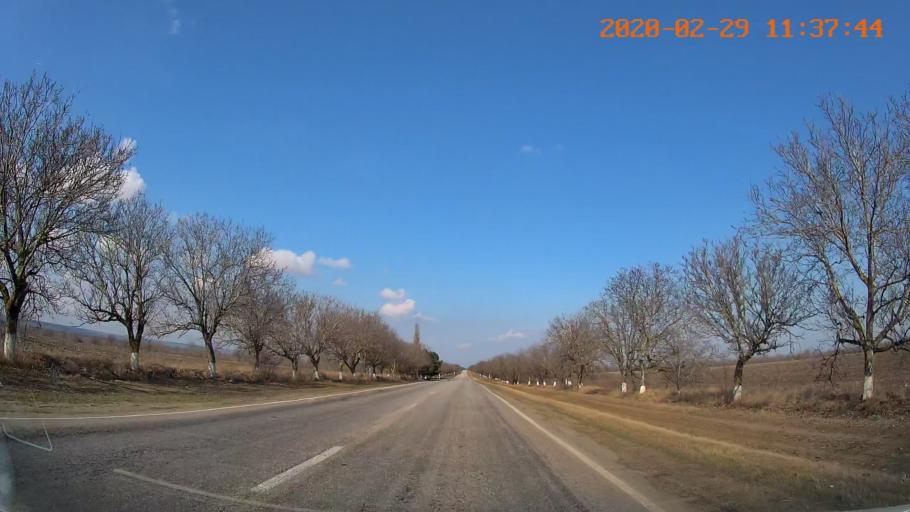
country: MD
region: Rezina
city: Saharna
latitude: 47.6157
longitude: 29.0434
